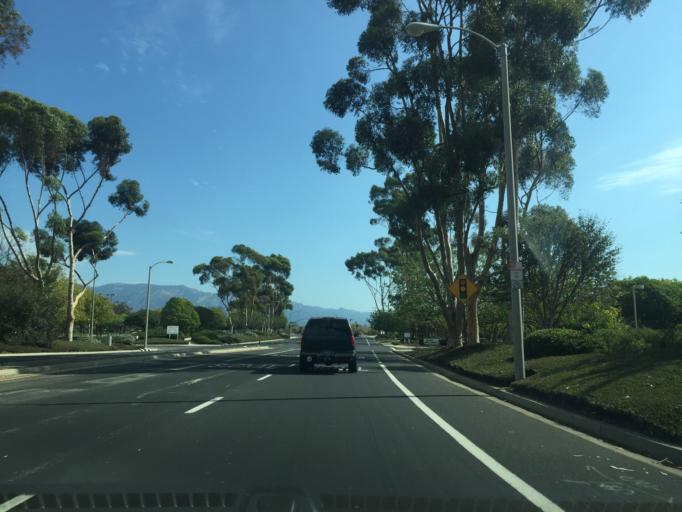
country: US
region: California
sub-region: Santa Barbara County
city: Isla Vista
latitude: 34.4327
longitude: -119.8577
